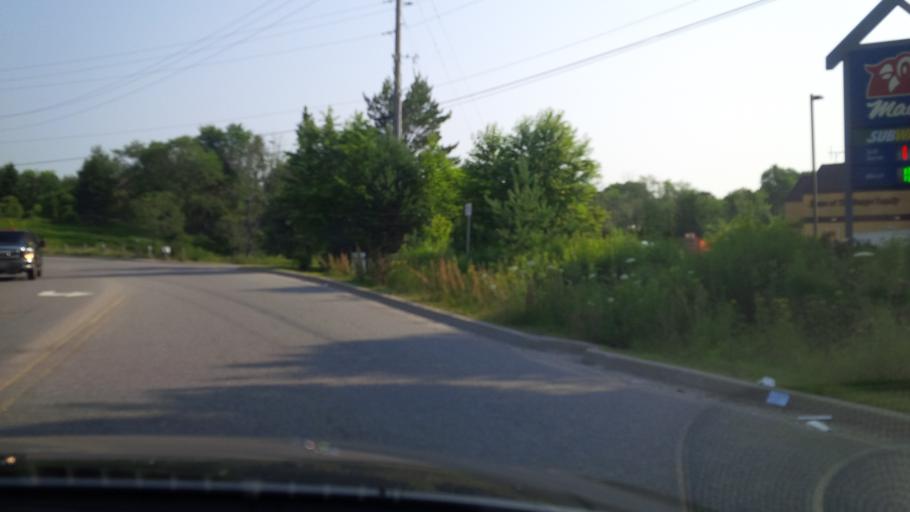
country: CA
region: Ontario
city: Huntsville
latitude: 45.3315
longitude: -79.2336
